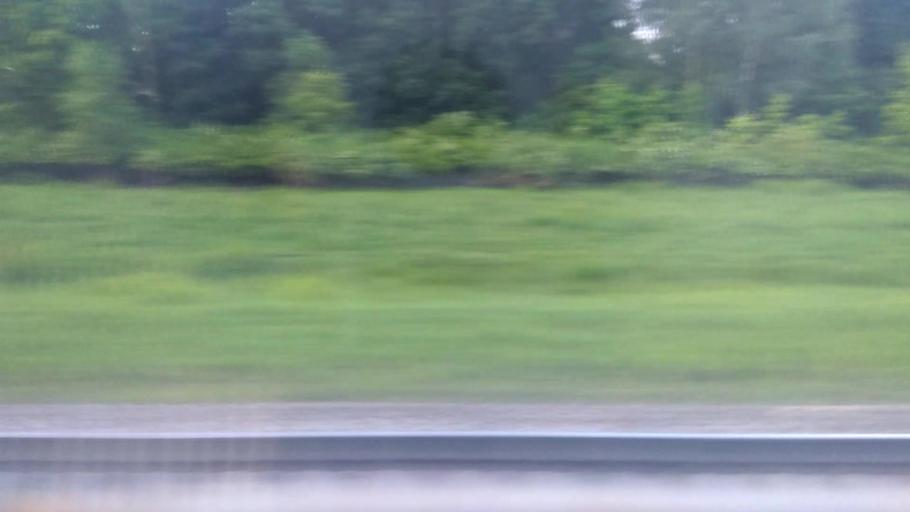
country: RU
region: Moskovskaya
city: Vostryakovo
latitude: 55.4010
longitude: 37.8009
